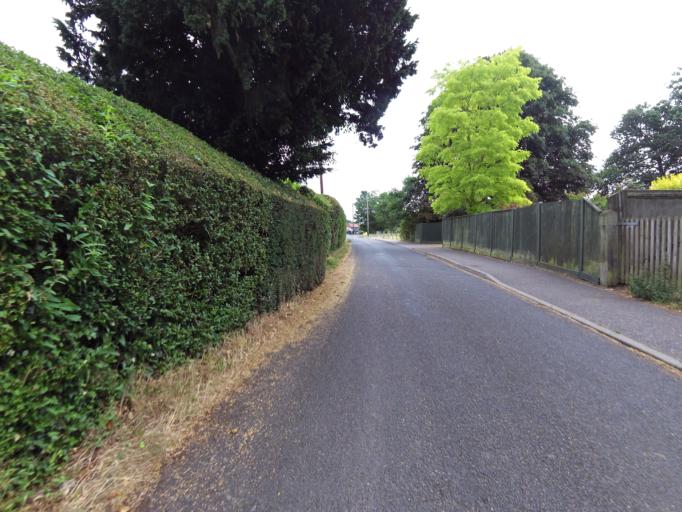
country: GB
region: England
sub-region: Norfolk
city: Harleston
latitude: 52.4027
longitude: 1.3039
